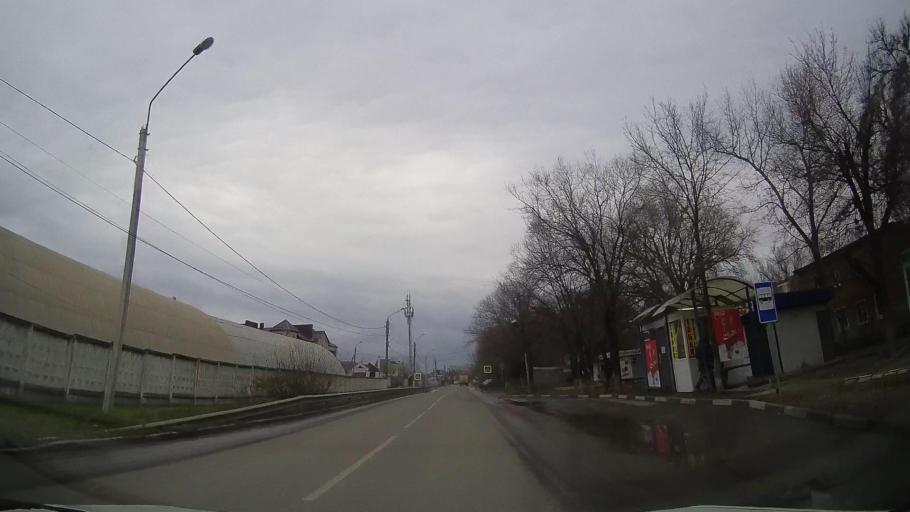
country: RU
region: Rostov
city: Bataysk
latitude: 47.1313
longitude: 39.7428
